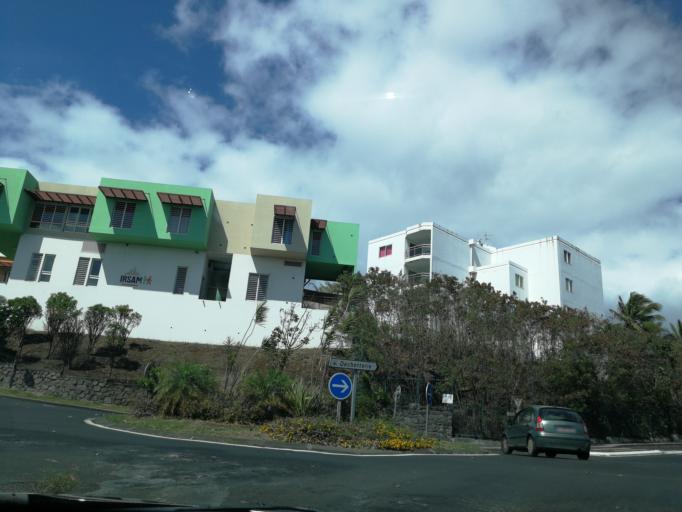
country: RE
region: Reunion
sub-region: Reunion
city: Saint-Denis
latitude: -20.9061
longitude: 55.4822
